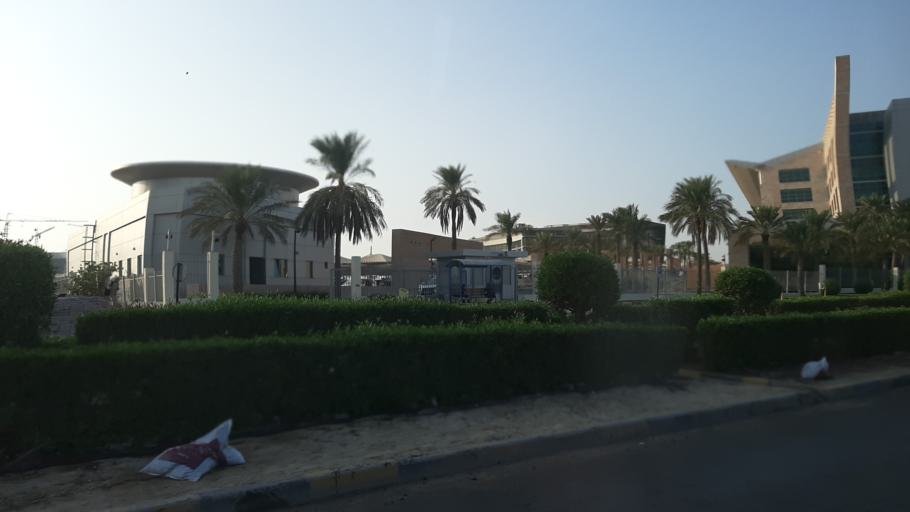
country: KW
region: Al Ahmadi
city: Al Ahmadi
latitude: 29.0914
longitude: 48.0882
